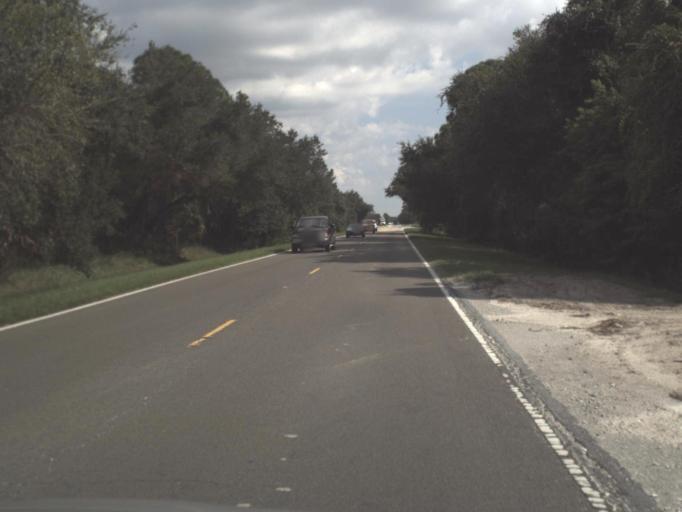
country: US
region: Florida
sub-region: Sarasota County
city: Plantation
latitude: 27.0933
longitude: -82.3399
